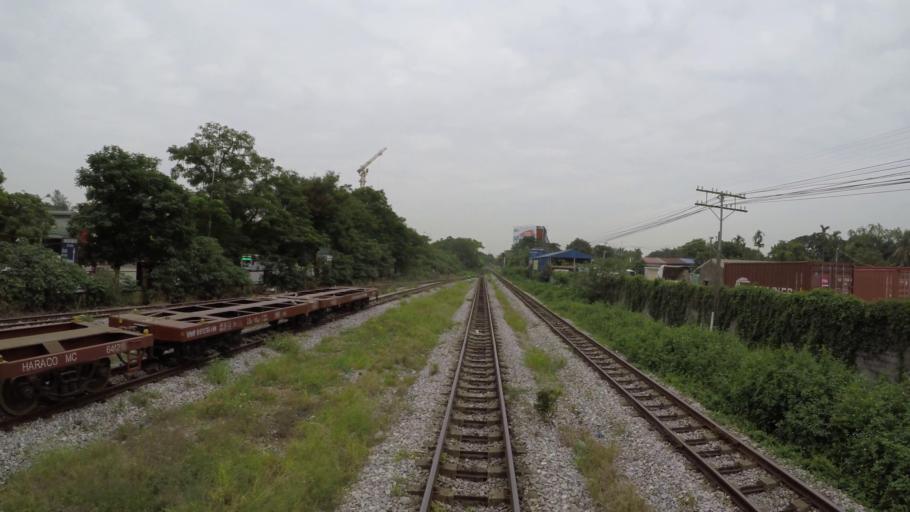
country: VN
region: Hai Phong
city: An Duong
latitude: 20.8788
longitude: 106.6265
